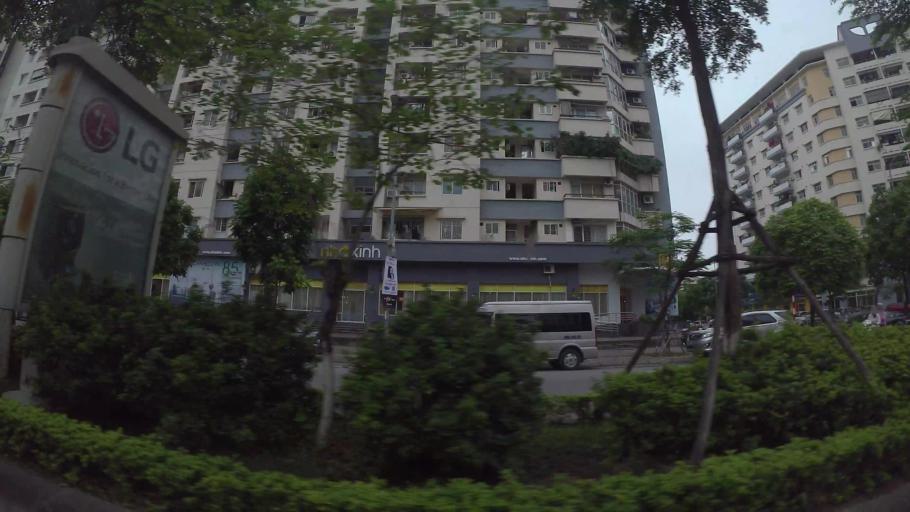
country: VN
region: Ha Noi
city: Cau Giay
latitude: 21.0176
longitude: 105.7936
